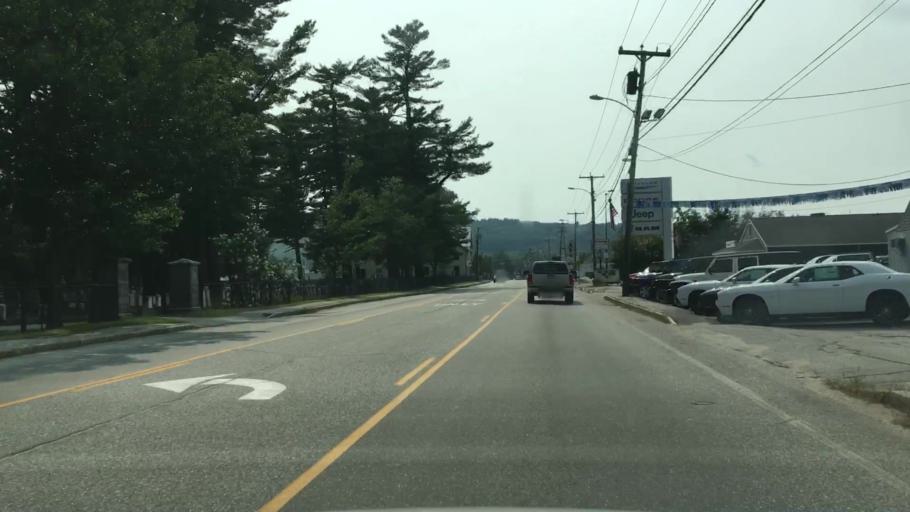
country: US
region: Maine
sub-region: Oxford County
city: South Paris
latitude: 44.2141
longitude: -70.5230
